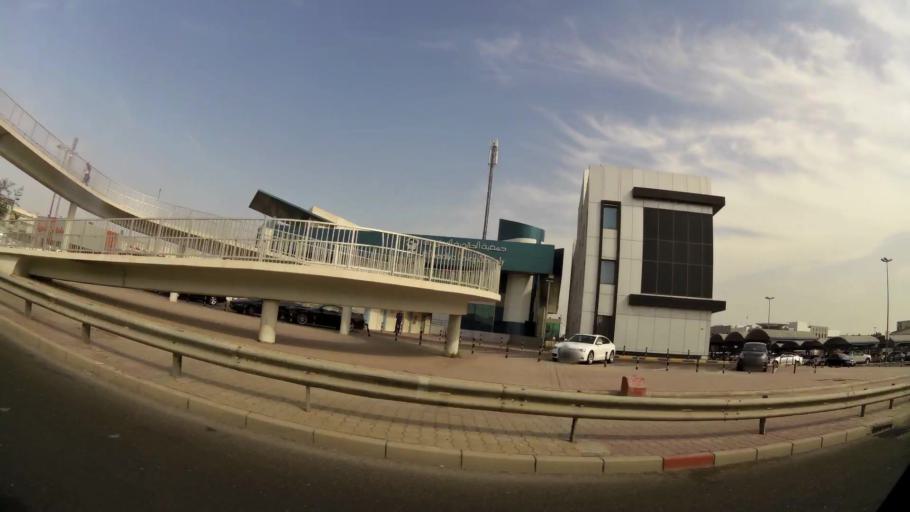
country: KW
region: Al Asimah
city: Ash Shamiyah
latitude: 29.3285
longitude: 47.9620
